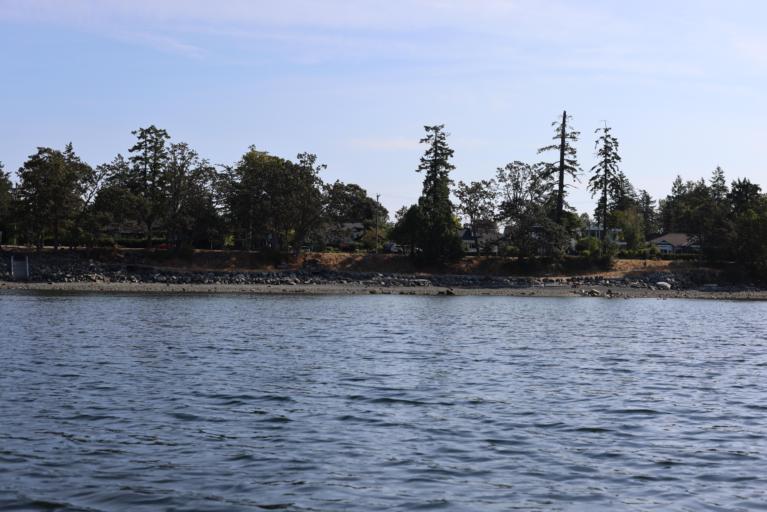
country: CA
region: British Columbia
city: North Saanich
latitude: 48.6585
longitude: -123.4505
